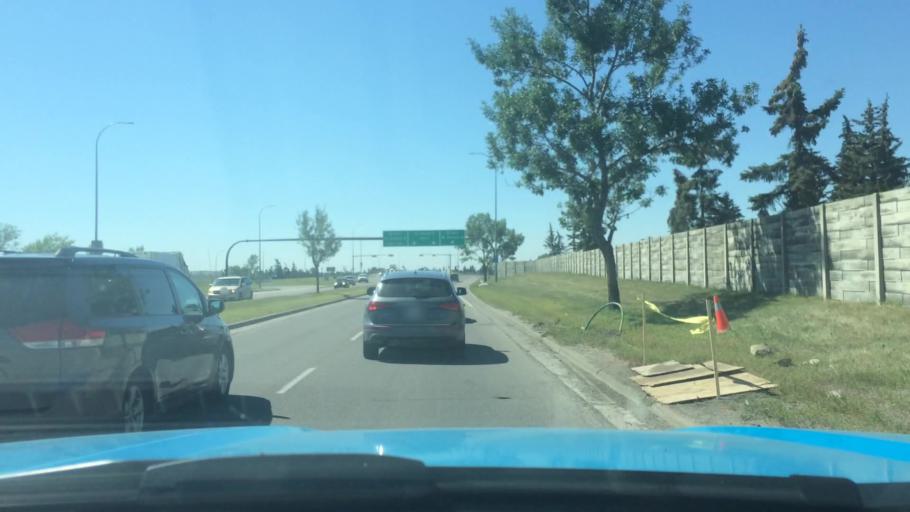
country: CA
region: Alberta
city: Calgary
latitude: 51.0704
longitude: -113.9585
